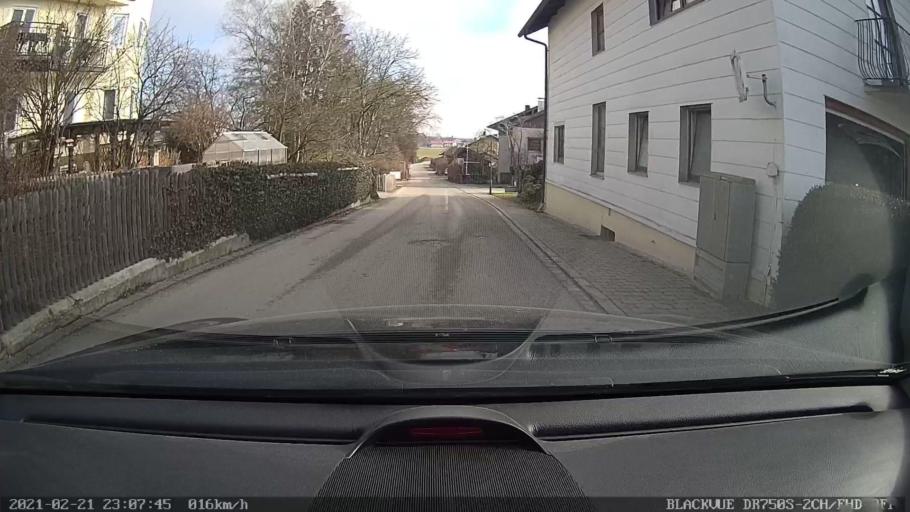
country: DE
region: Bavaria
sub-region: Upper Bavaria
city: Griesstatt
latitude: 47.9942
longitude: 12.1799
